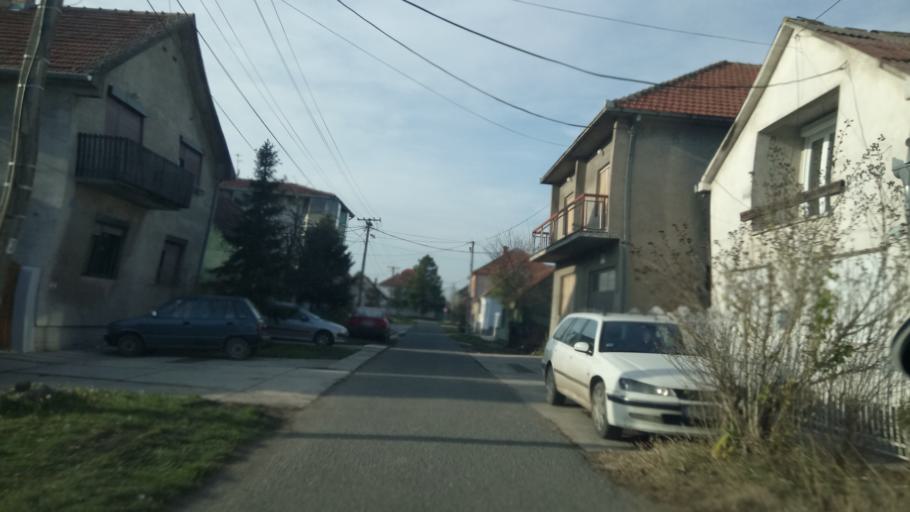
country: RS
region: Autonomna Pokrajina Vojvodina
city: Nova Pazova
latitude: 44.9484
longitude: 20.2302
